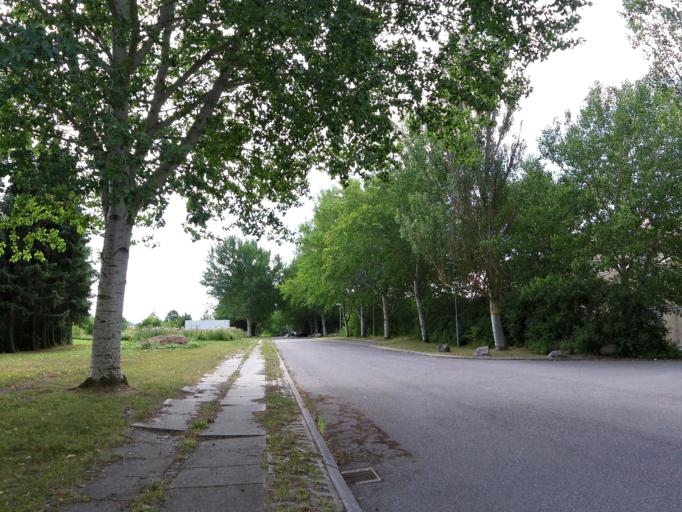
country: DK
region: Capital Region
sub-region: Fredensborg Kommune
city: Niva
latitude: 55.9392
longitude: 12.4853
